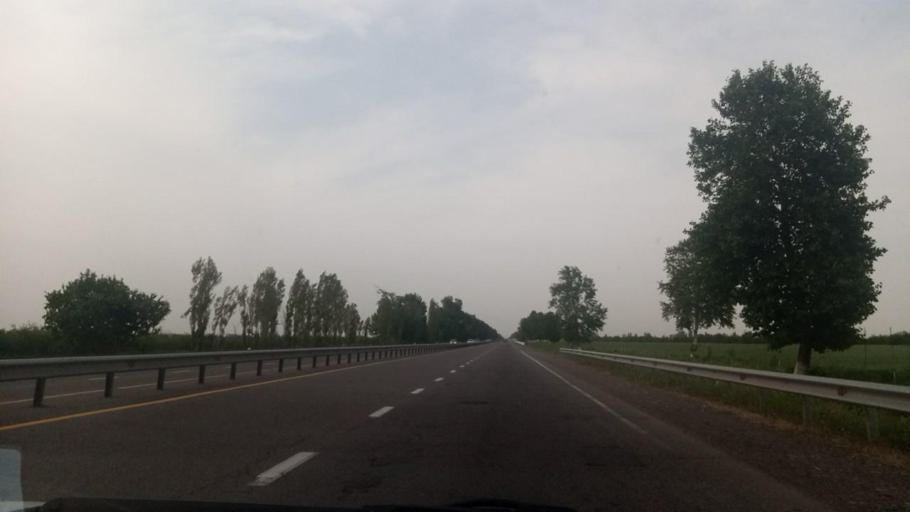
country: UZ
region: Toshkent Shahri
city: Bektemir
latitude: 41.1957
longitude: 69.4032
